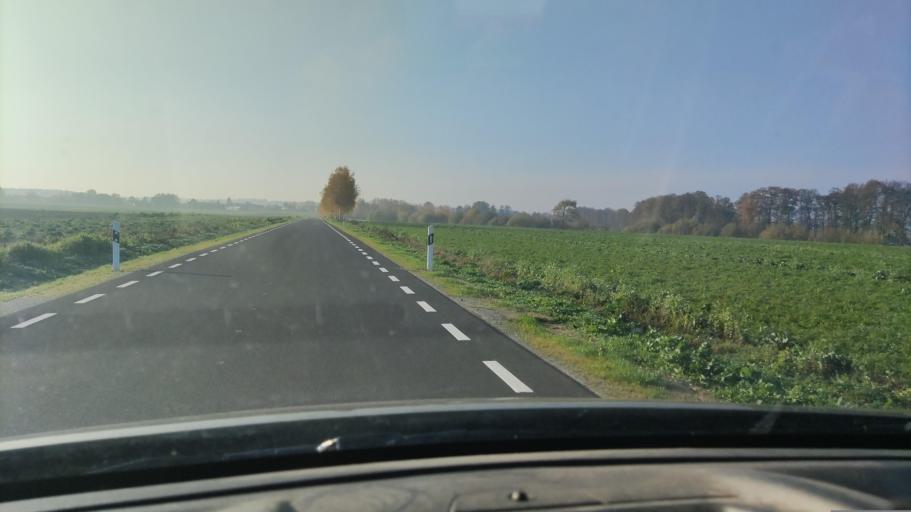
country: DE
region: Mecklenburg-Vorpommern
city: Wesenberg
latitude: 53.2260
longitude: 13.0502
